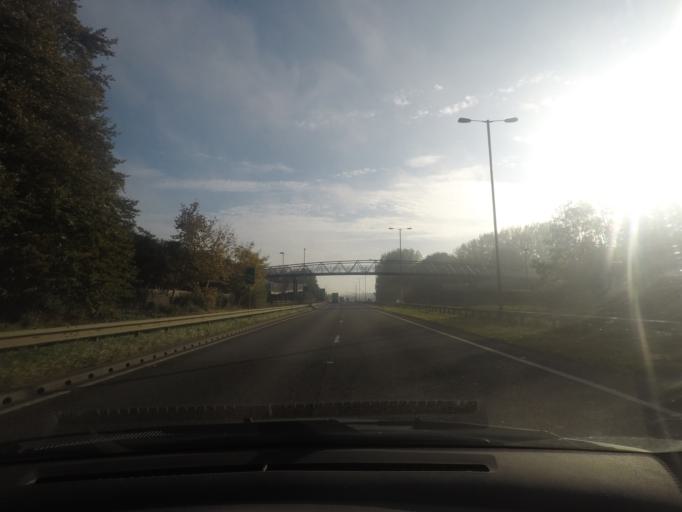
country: GB
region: England
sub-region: East Riding of Yorkshire
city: Welton
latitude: 53.7256
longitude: -0.5311
